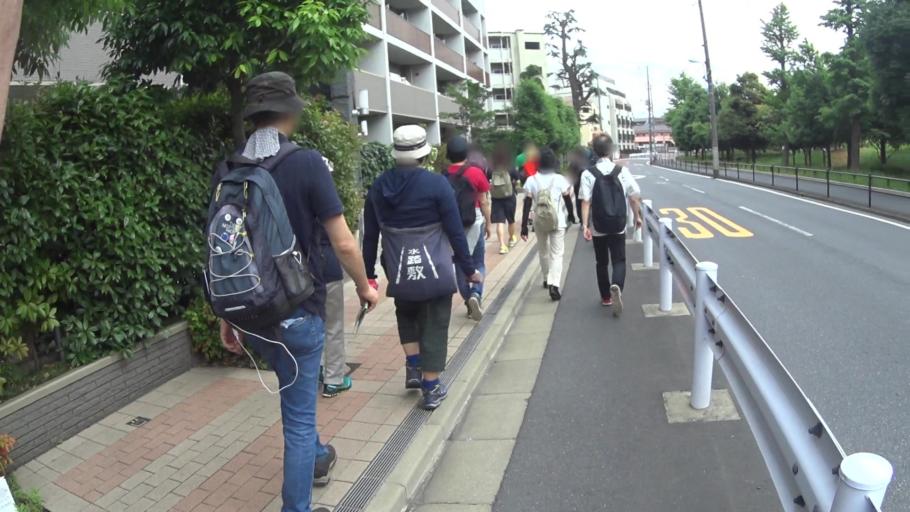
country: JP
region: Tokyo
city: Musashino
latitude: 35.7142
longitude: 139.6077
